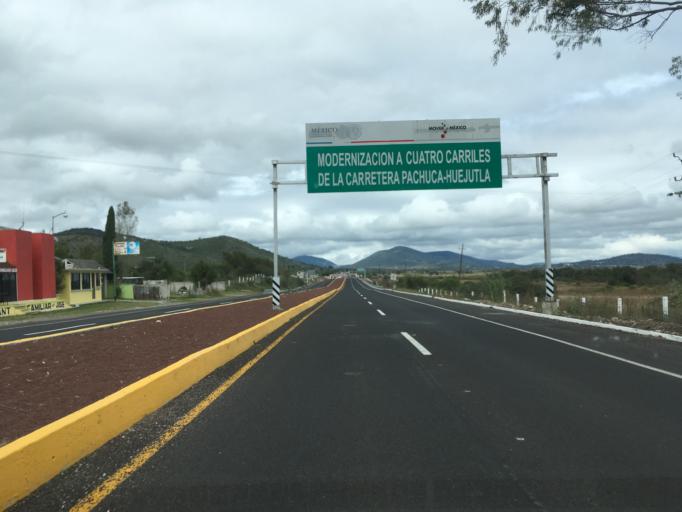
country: MX
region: Hidalgo
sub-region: Atotonilco el Grande
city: Santa Maria Amajac
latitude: 20.3423
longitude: -98.7092
